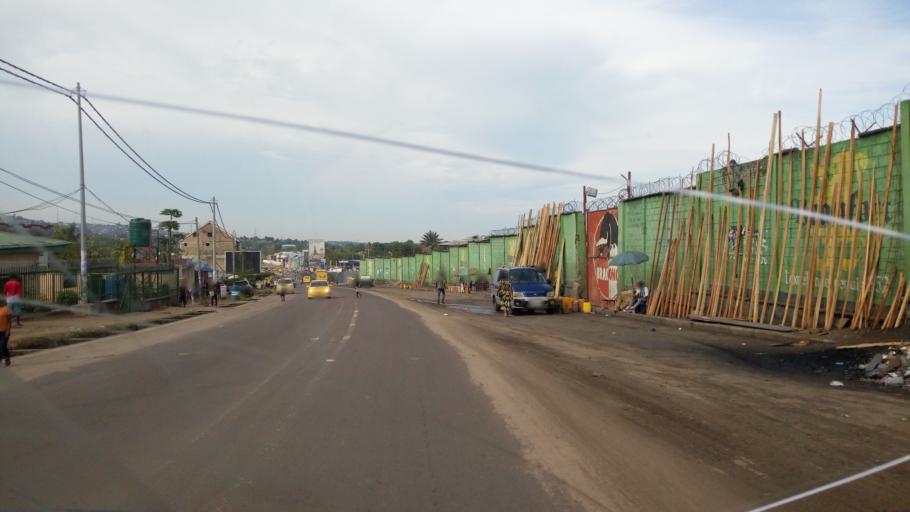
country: CD
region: Kinshasa
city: Kinshasa
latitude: -4.4421
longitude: 15.2558
